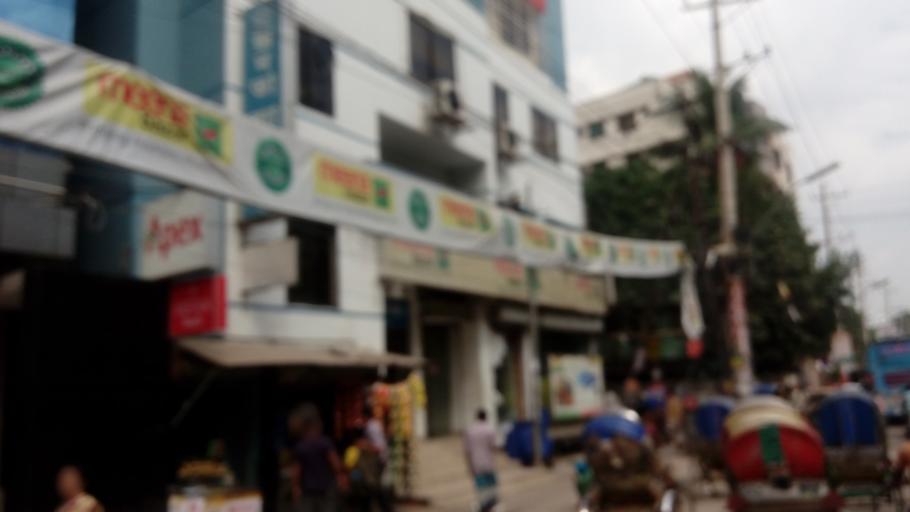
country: BD
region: Dhaka
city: Azimpur
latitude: 23.7585
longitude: 90.3639
